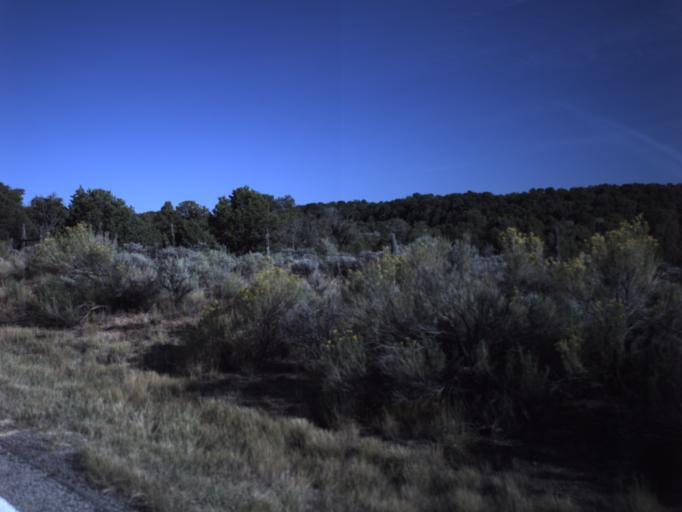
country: US
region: Utah
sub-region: Grand County
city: Moab
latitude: 38.3192
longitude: -109.3315
